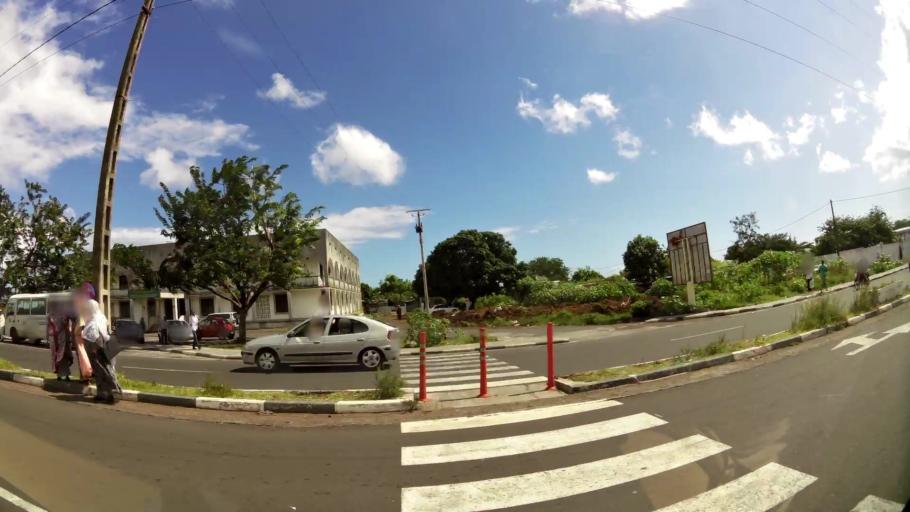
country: KM
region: Grande Comore
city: Mavingouni
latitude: -11.7175
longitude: 43.2456
